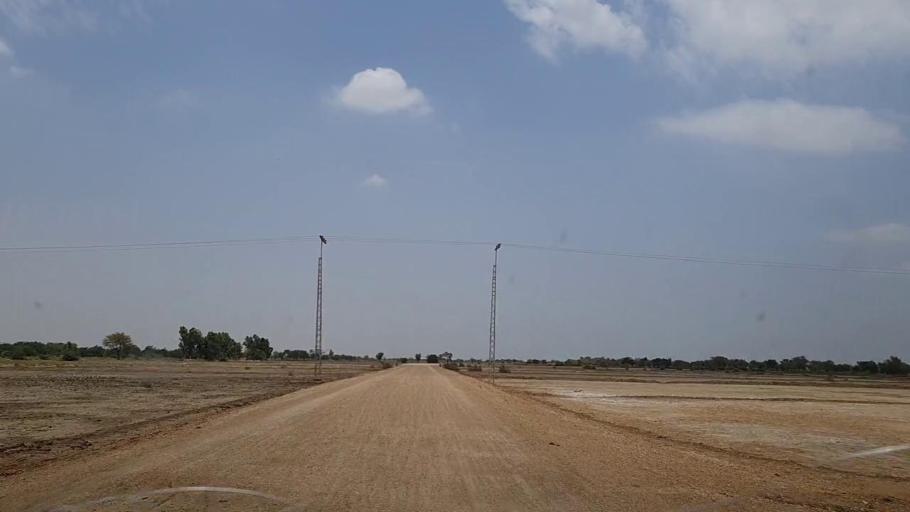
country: PK
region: Sindh
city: Phulji
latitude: 26.8174
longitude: 67.6340
